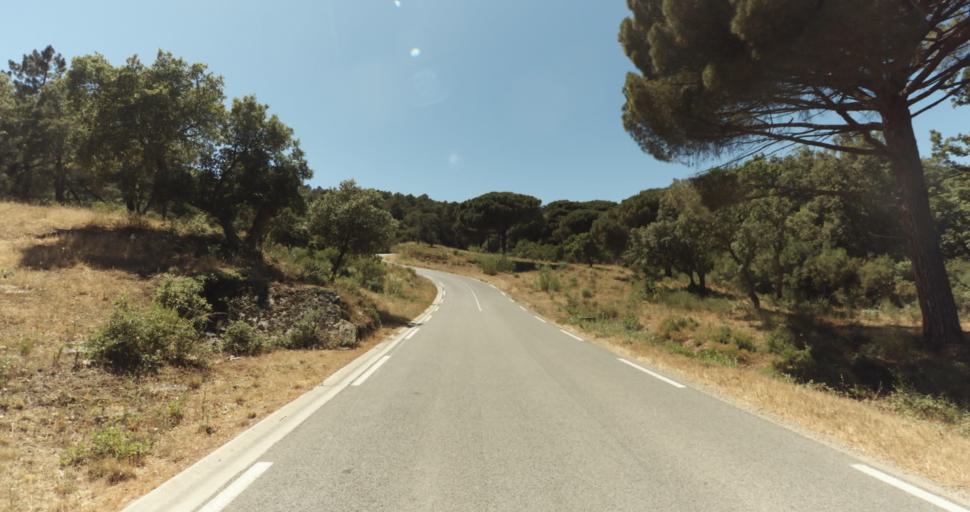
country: FR
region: Provence-Alpes-Cote d'Azur
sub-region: Departement du Var
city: Gassin
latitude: 43.2396
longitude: 6.5653
